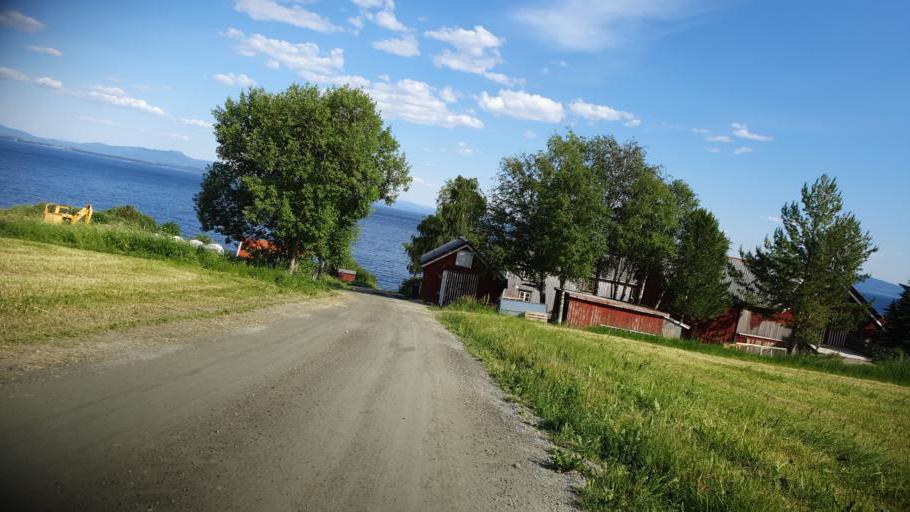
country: NO
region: Sor-Trondelag
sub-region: Trondheim
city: Trondheim
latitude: 63.5825
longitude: 10.4148
